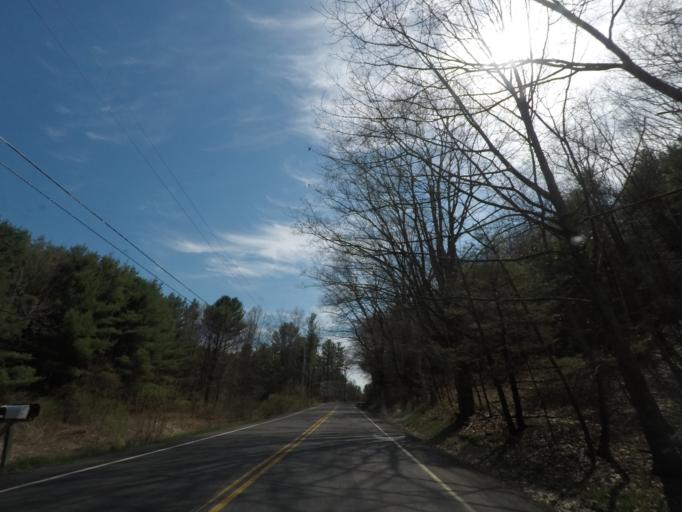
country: US
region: New York
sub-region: Columbia County
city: Chatham
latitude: 42.3763
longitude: -73.5296
